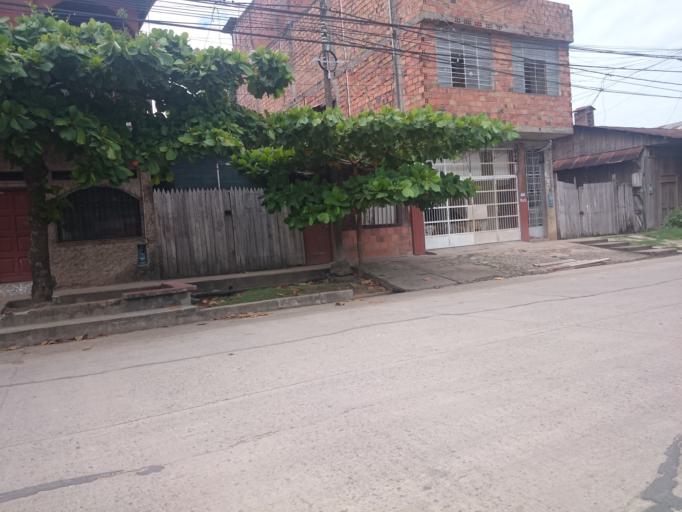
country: PE
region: Ucayali
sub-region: Provincia de Coronel Portillo
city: Pucallpa
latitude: -8.3787
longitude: -74.5303
